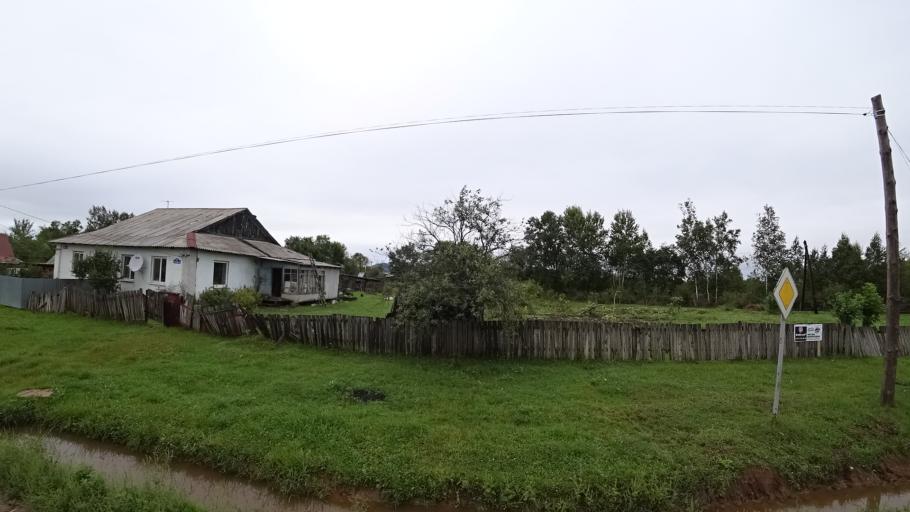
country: RU
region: Primorskiy
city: Monastyrishche
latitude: 44.0774
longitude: 132.5883
